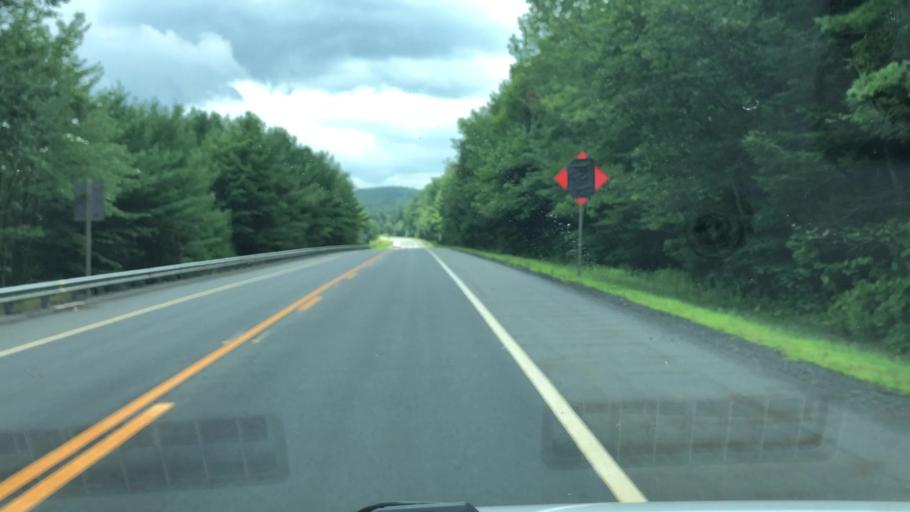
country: US
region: Massachusetts
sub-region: Franklin County
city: Ashfield
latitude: 42.4748
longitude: -72.8102
